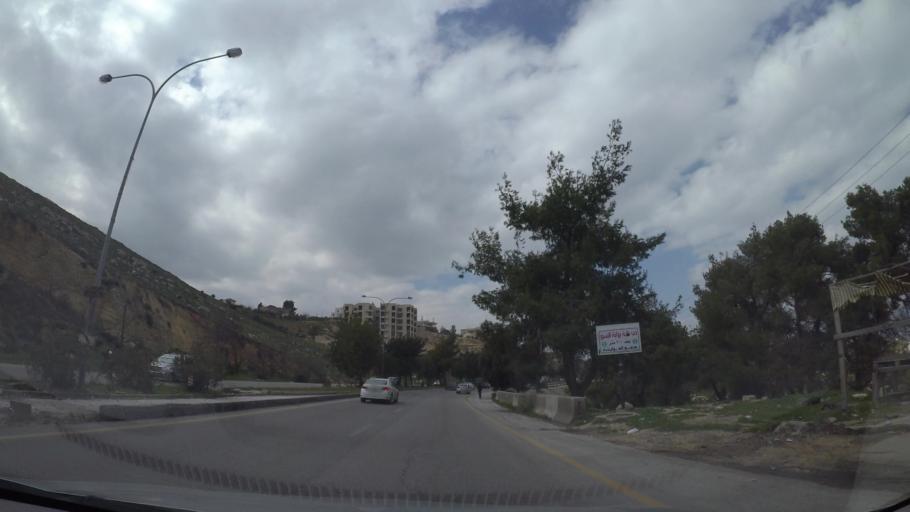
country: JO
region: Balqa
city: As Salt
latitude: 32.0305
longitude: 35.7953
